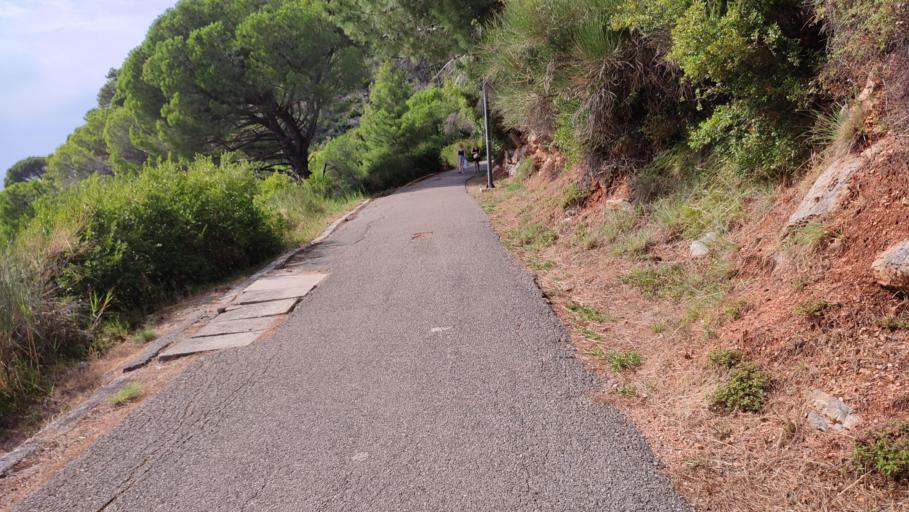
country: ME
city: Petrovac na Moru
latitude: 42.2067
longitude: 18.9328
